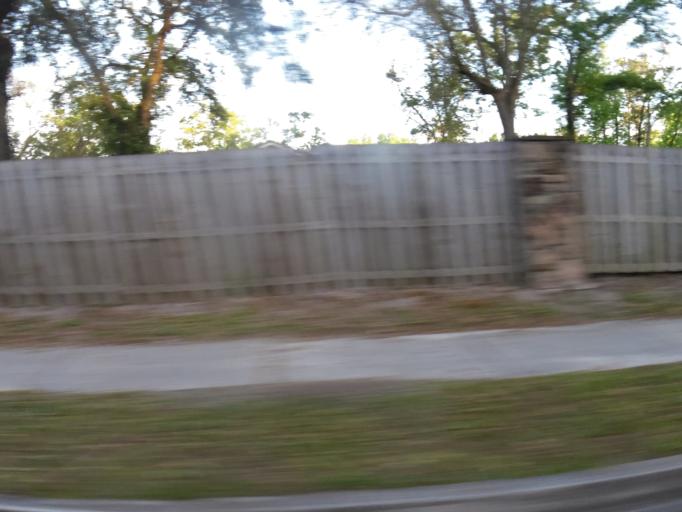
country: US
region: Florida
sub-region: Duval County
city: Jacksonville
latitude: 30.2624
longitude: -81.5764
